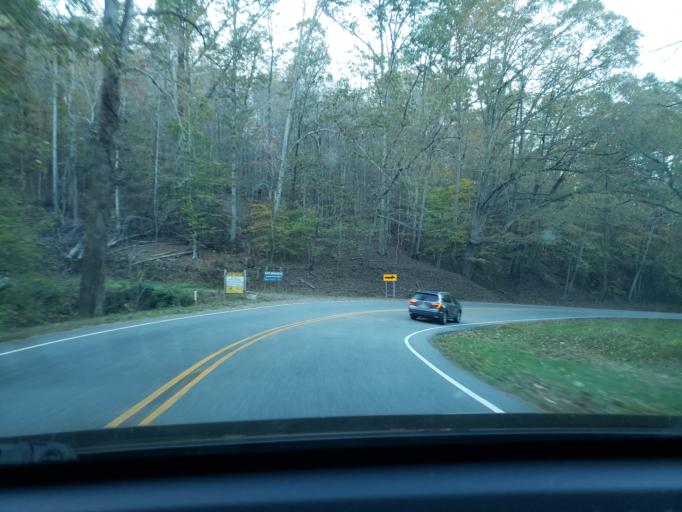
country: US
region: North Carolina
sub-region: Stokes County
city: Danbury
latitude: 36.4021
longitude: -80.2028
